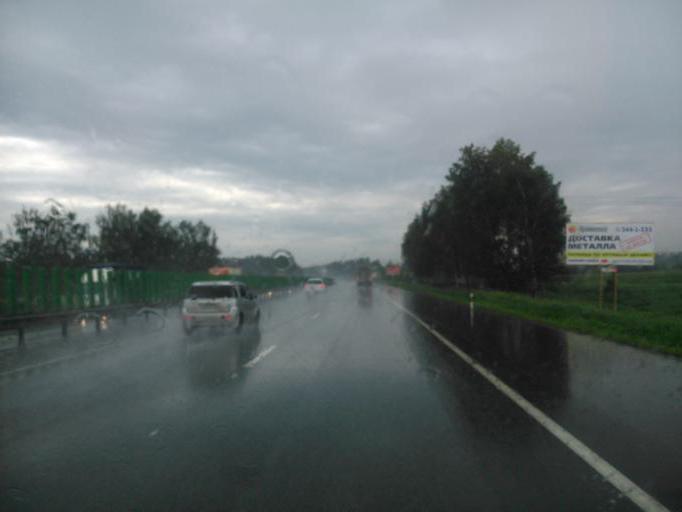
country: RU
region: Sverdlovsk
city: Istok
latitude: 56.7907
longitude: 60.8295
